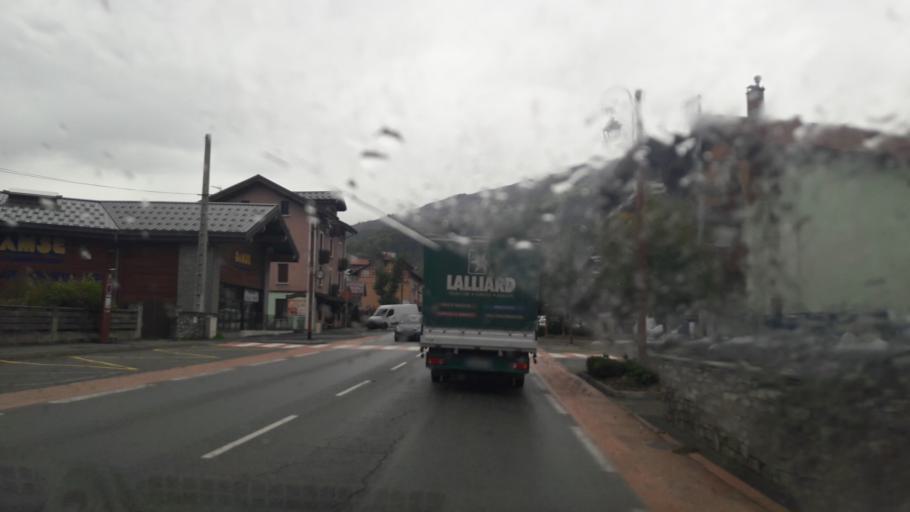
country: FR
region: Rhone-Alpes
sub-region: Departement de la Savoie
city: Bourg-Saint-Maurice
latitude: 45.6216
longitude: 6.7741
